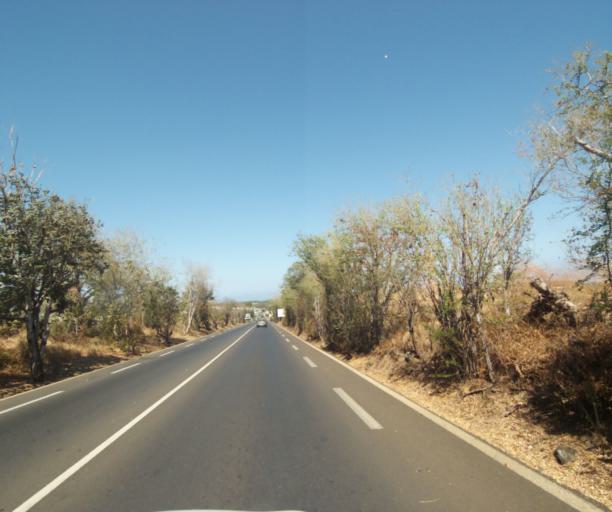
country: RE
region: Reunion
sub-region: Reunion
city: Saint-Paul
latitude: -20.9842
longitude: 55.3010
